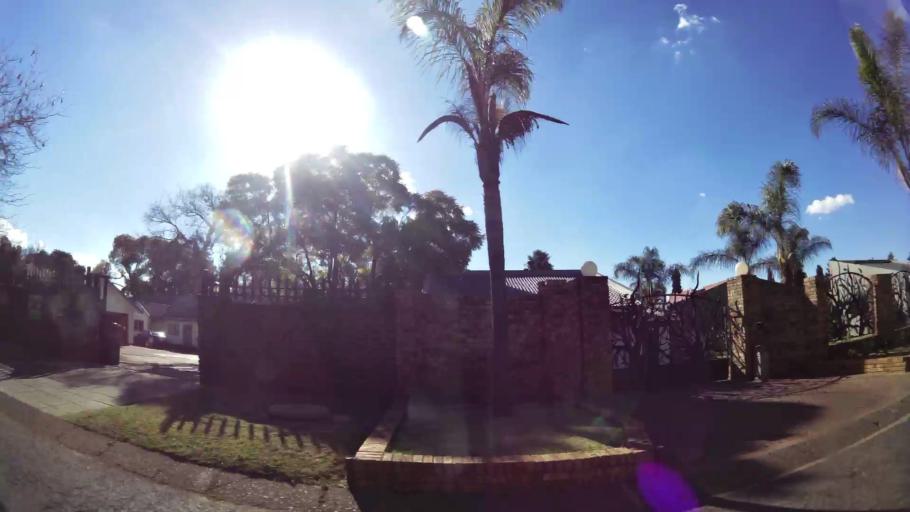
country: ZA
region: Gauteng
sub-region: West Rand District Municipality
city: Carletonville
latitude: -26.3721
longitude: 27.4077
